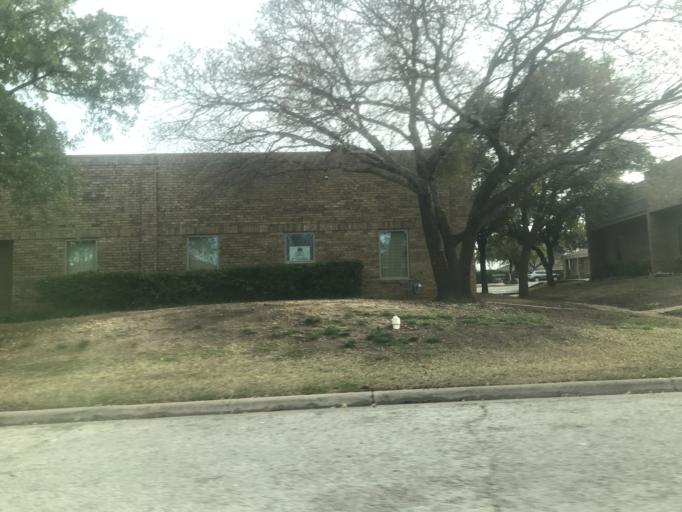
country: US
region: Texas
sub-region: Taylor County
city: Abilene
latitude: 32.3943
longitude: -99.7618
